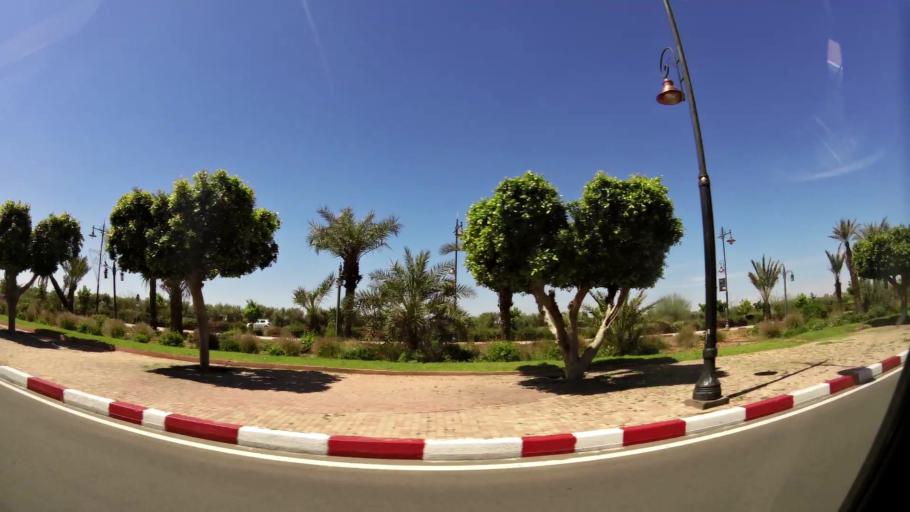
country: MA
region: Marrakech-Tensift-Al Haouz
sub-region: Marrakech
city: Marrakesh
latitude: 31.6171
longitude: -7.9967
